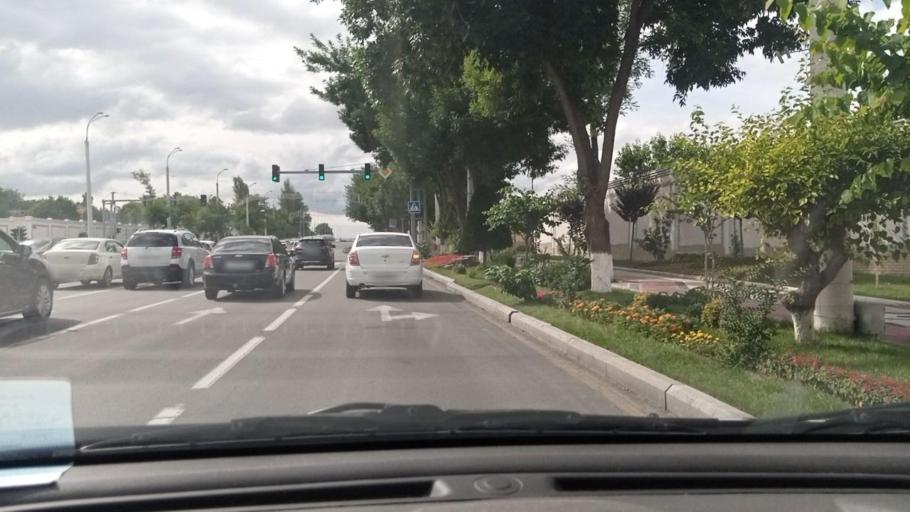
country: UZ
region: Toshkent
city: Salor
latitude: 41.3287
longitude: 69.3554
